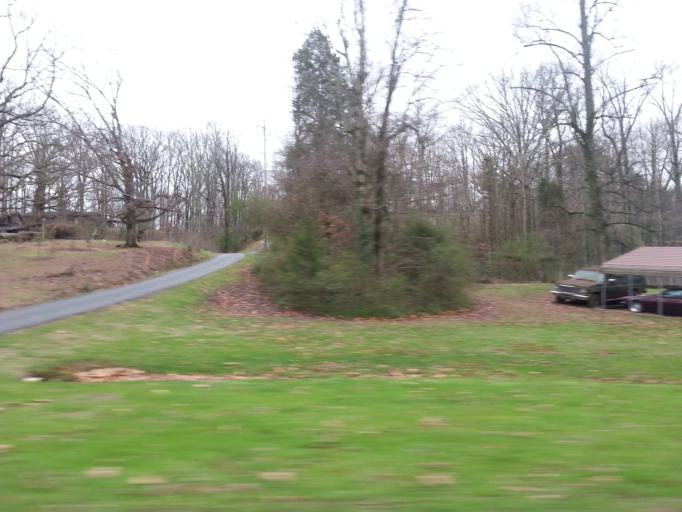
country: US
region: Tennessee
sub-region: Knox County
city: Knoxville
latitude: 35.9927
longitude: -84.0266
